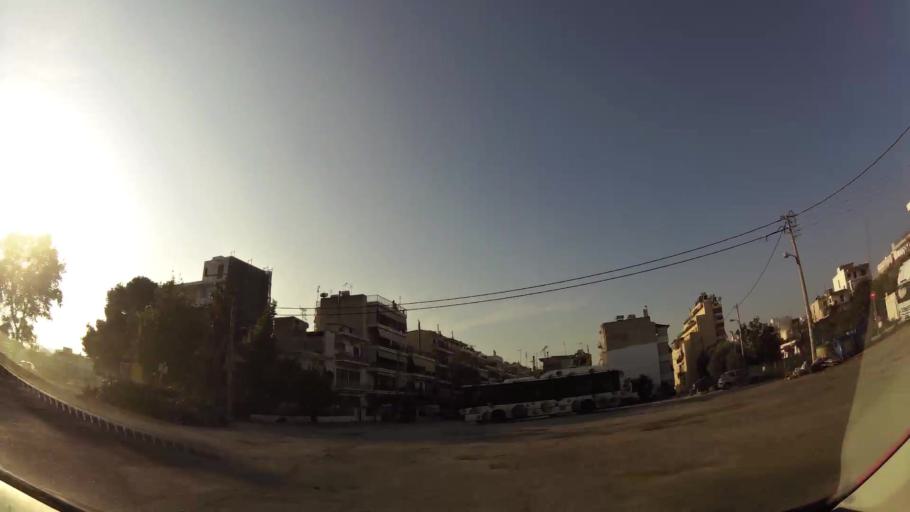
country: GR
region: Attica
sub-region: Nomarchia Athinas
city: Nea Filadelfeia
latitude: 38.0478
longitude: 23.7345
